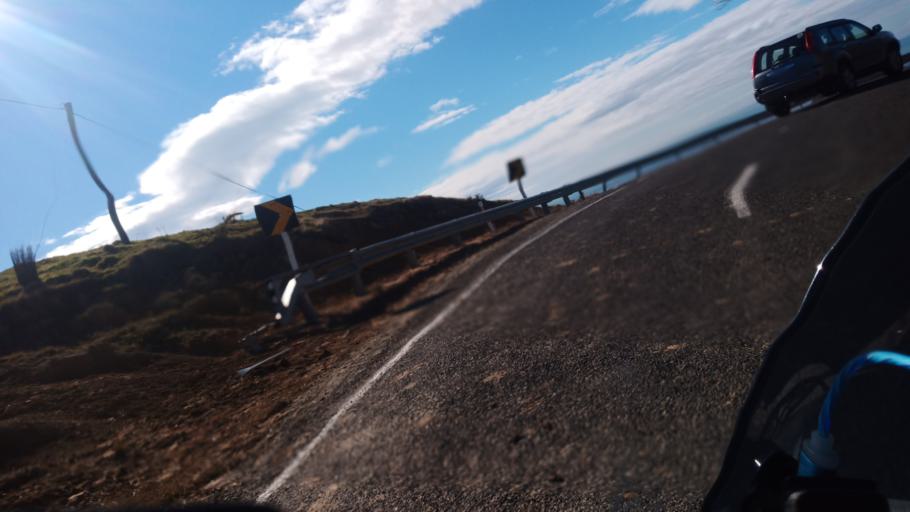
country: NZ
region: Gisborne
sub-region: Gisborne District
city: Gisborne
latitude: -38.2490
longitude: 178.3035
